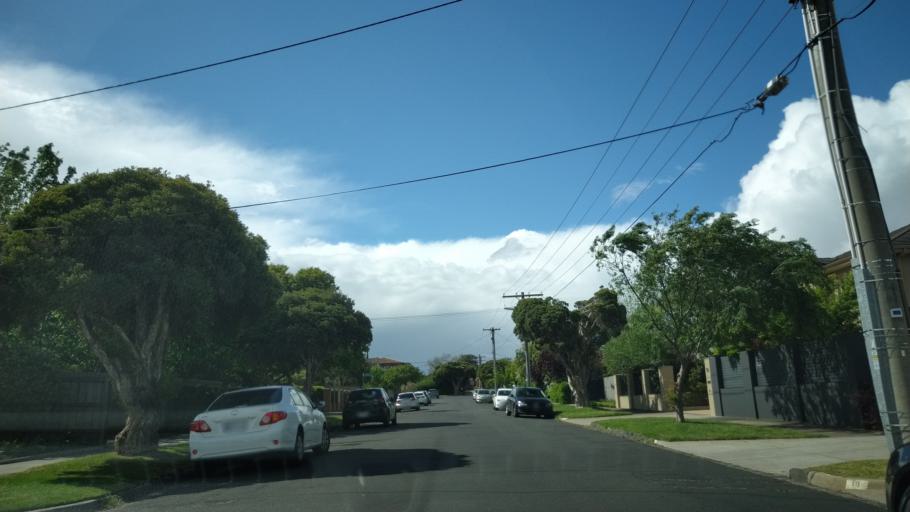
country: AU
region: Victoria
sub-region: Glen Eira
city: Caulfield
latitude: -37.8793
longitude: 145.0270
